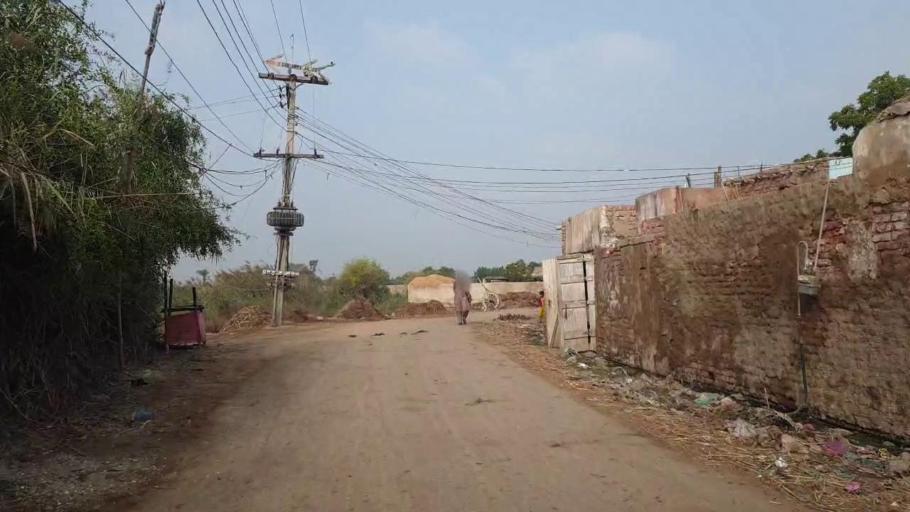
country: PK
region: Sindh
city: Tando Muhammad Khan
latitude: 25.1291
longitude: 68.5921
